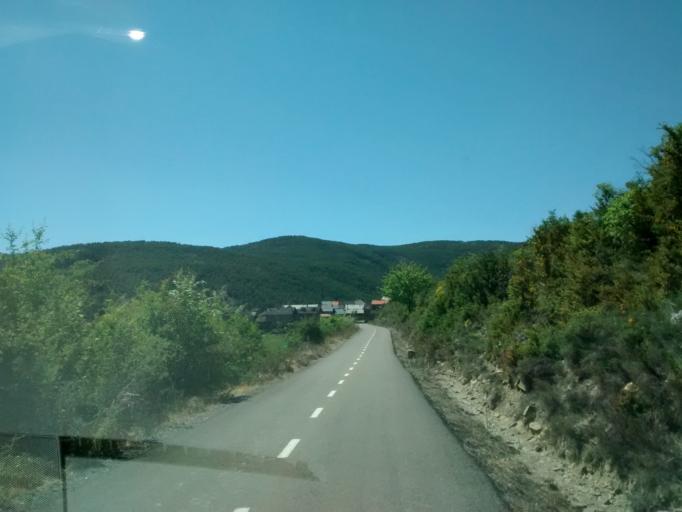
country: ES
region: Aragon
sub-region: Provincia de Huesca
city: Borau
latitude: 42.6780
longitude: -0.6167
